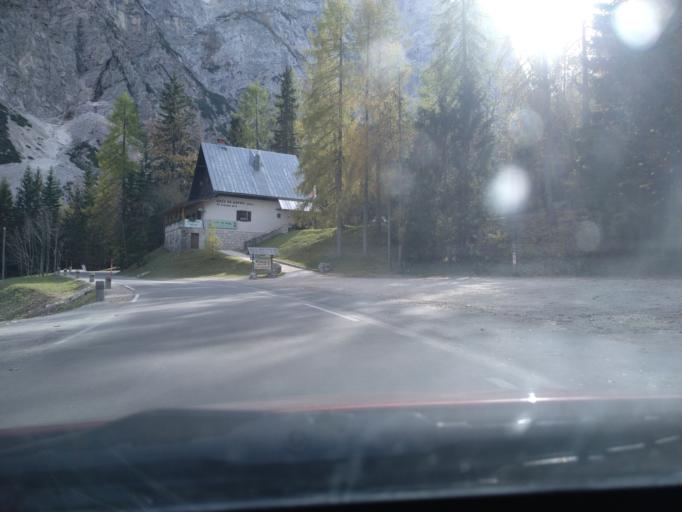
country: SI
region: Kranjska Gora
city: Kranjska Gora
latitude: 46.4401
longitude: 13.7625
